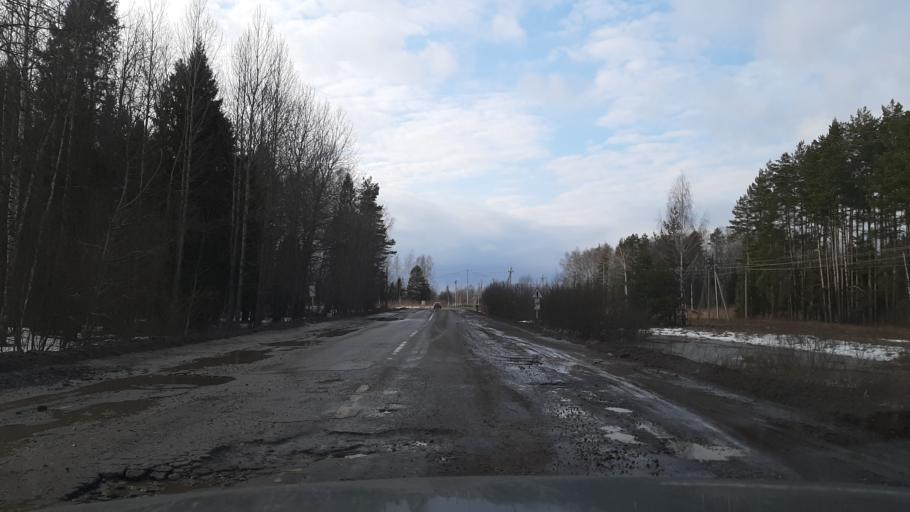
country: RU
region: Ivanovo
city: Novo-Talitsy
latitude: 56.9374
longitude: 40.7252
